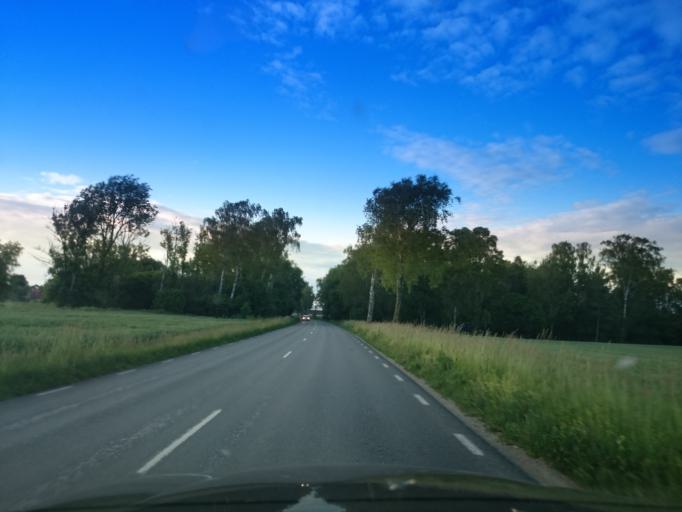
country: SE
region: Gotland
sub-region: Gotland
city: Hemse
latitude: 57.3159
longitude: 18.3845
